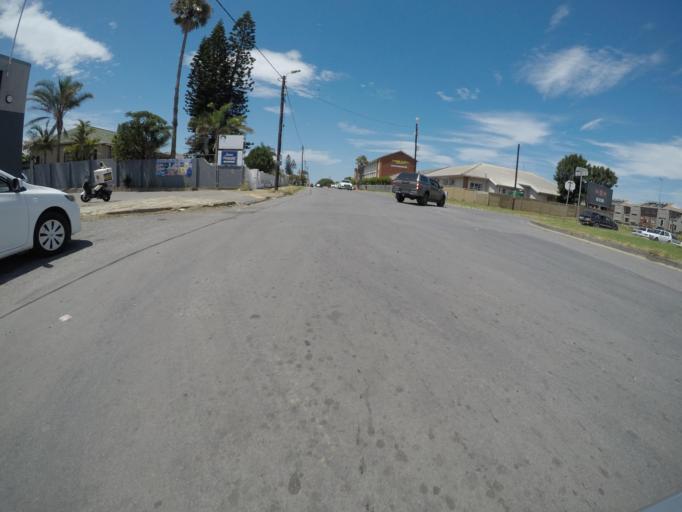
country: ZA
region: Eastern Cape
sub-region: Buffalo City Metropolitan Municipality
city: East London
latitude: -33.0355
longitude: 27.8555
